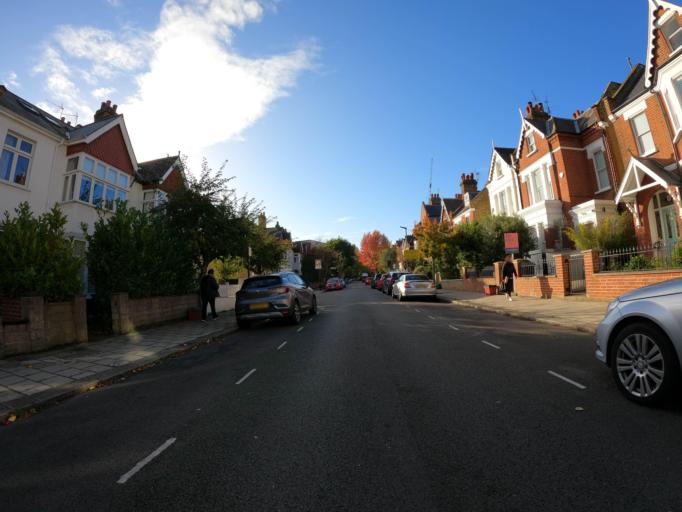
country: GB
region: England
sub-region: Greater London
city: Acton
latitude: 51.4892
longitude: -0.2833
